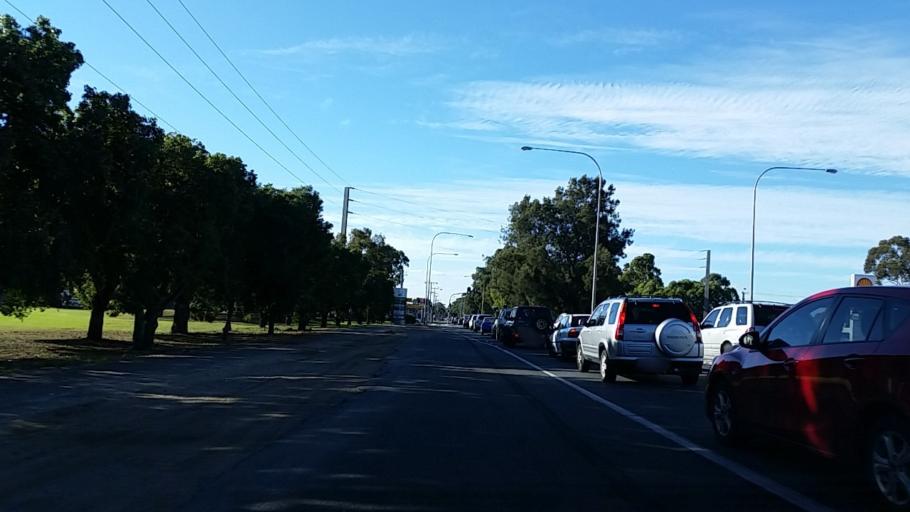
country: AU
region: South Australia
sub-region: Playford
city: Smithfield
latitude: -34.6850
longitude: 138.6923
